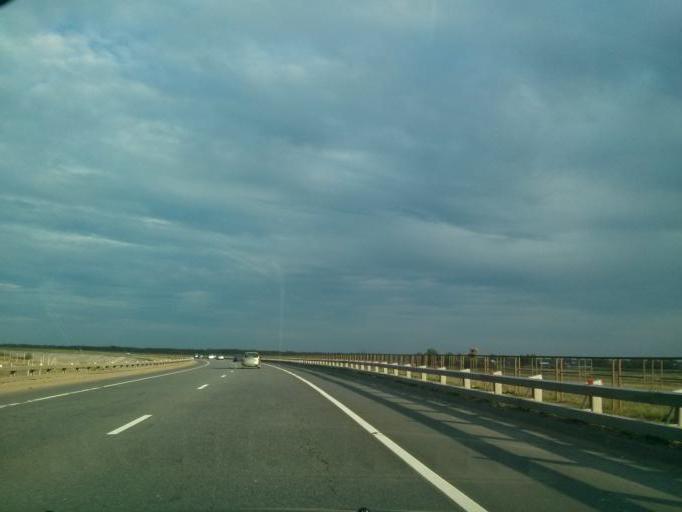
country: RU
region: Vladimir
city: Murom
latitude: 55.5894
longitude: 42.1210
